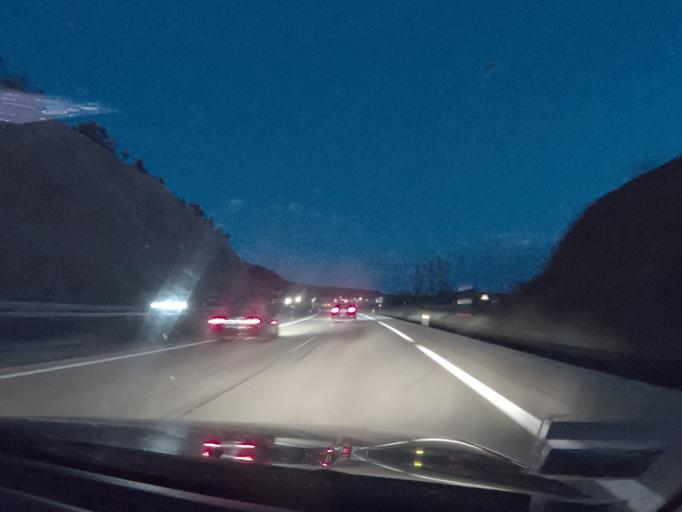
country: ES
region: Castille and Leon
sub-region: Provincia de Leon
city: Villagaton
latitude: 42.5933
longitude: -6.2206
